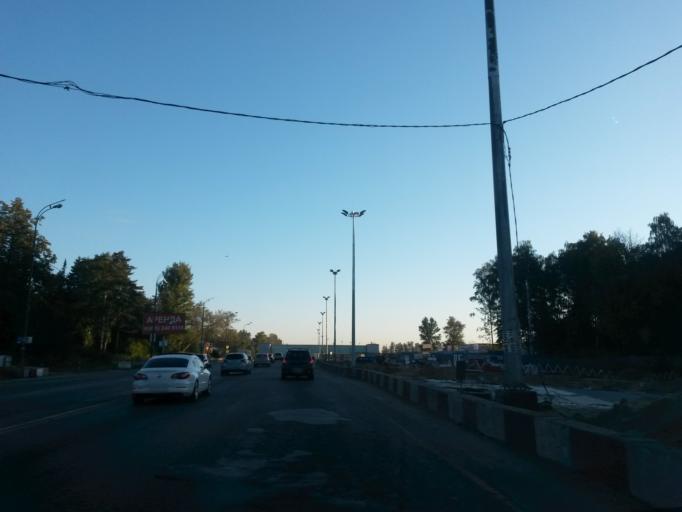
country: RU
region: Moskovskaya
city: Bolshevo
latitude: 55.9414
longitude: 37.8128
